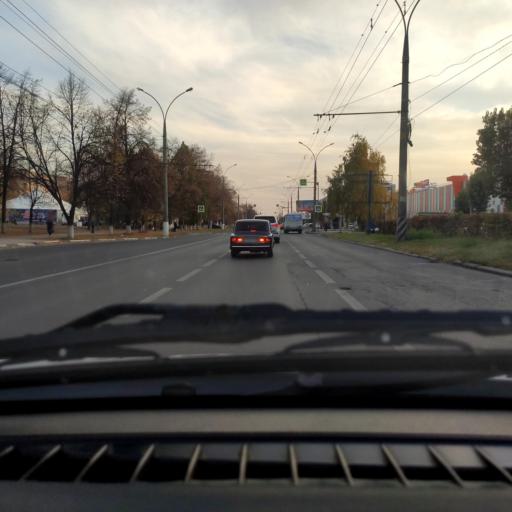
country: RU
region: Samara
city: Tol'yatti
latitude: 53.5316
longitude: 49.2768
